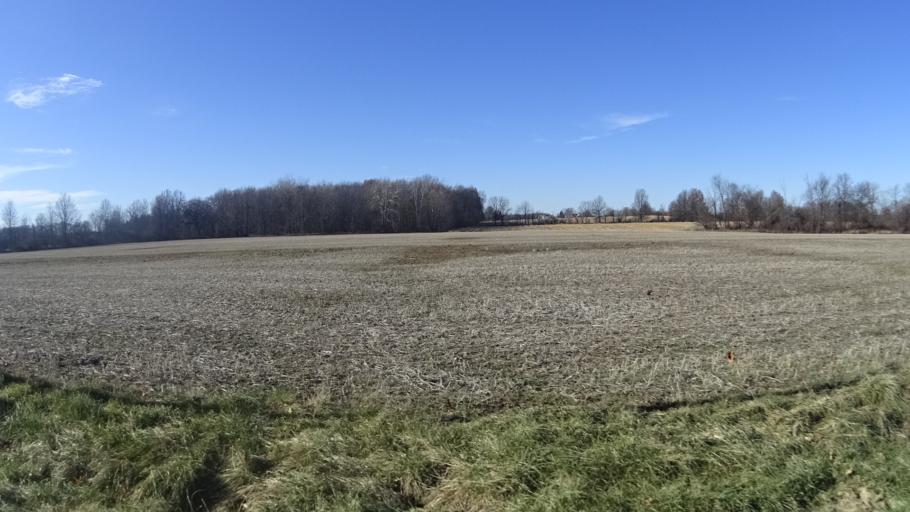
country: US
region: Ohio
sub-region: Lorain County
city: South Amherst
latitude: 41.3317
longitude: -82.2881
